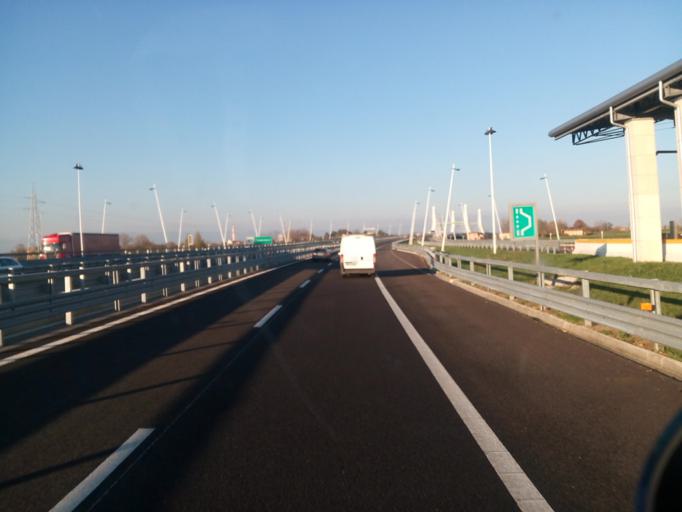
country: IT
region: Veneto
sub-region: Provincia di Vicenza
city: Villaganzerla
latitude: 45.4560
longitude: 11.6289
